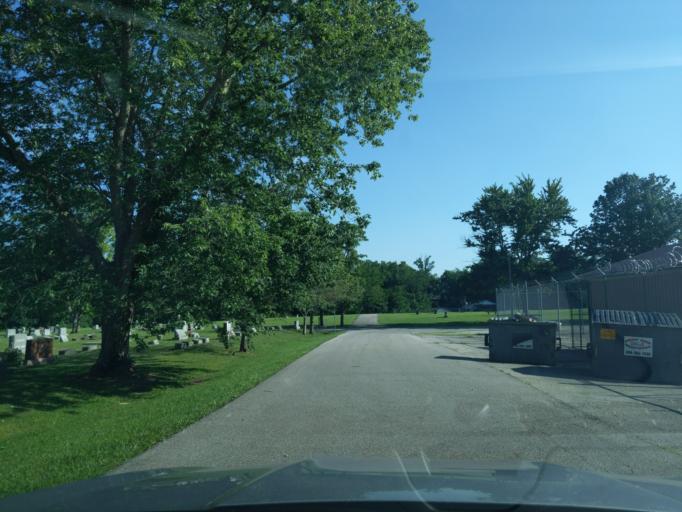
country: US
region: Indiana
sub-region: Ripley County
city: Versailles
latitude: 39.0727
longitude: -85.2486
